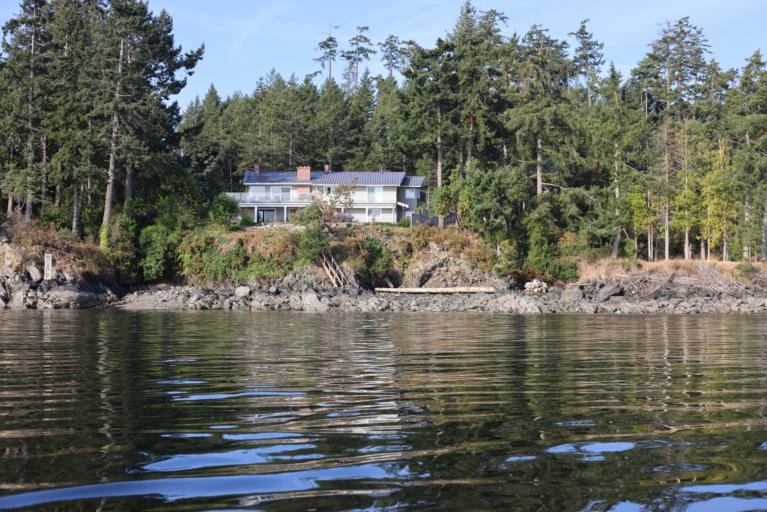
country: CA
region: British Columbia
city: North Saanich
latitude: 48.6886
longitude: -123.4011
